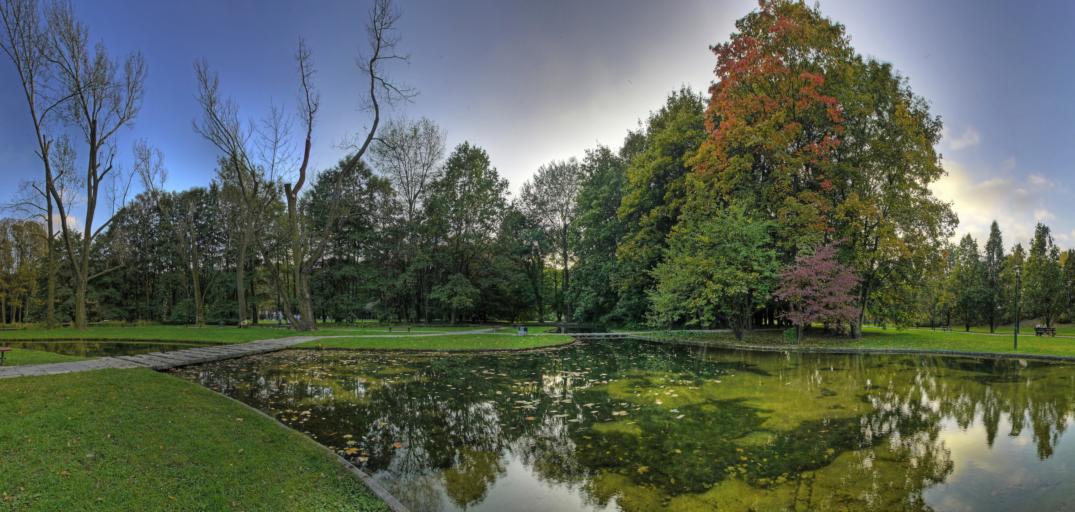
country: PL
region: Masovian Voivodeship
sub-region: Warszawa
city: Ochota
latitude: 52.2120
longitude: 21.0006
